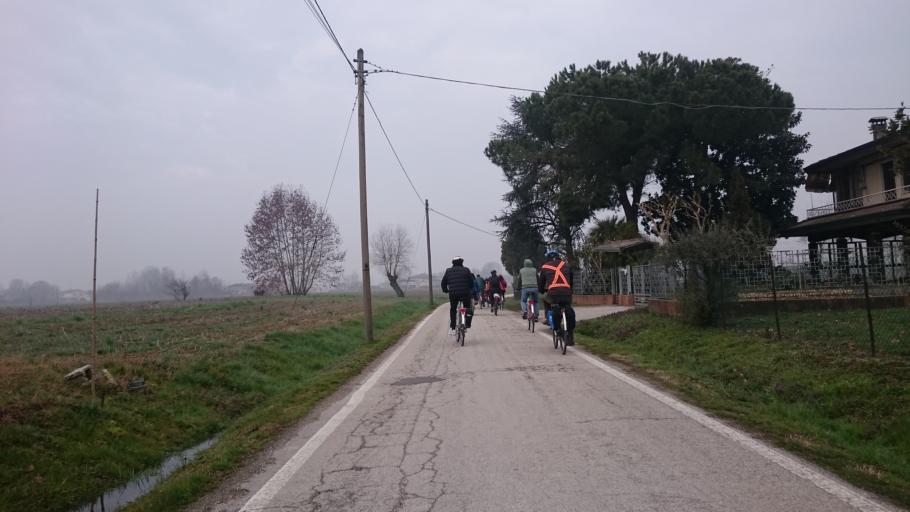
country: IT
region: Veneto
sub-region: Provincia di Vicenza
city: Montegalda
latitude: 45.4777
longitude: 11.6608
